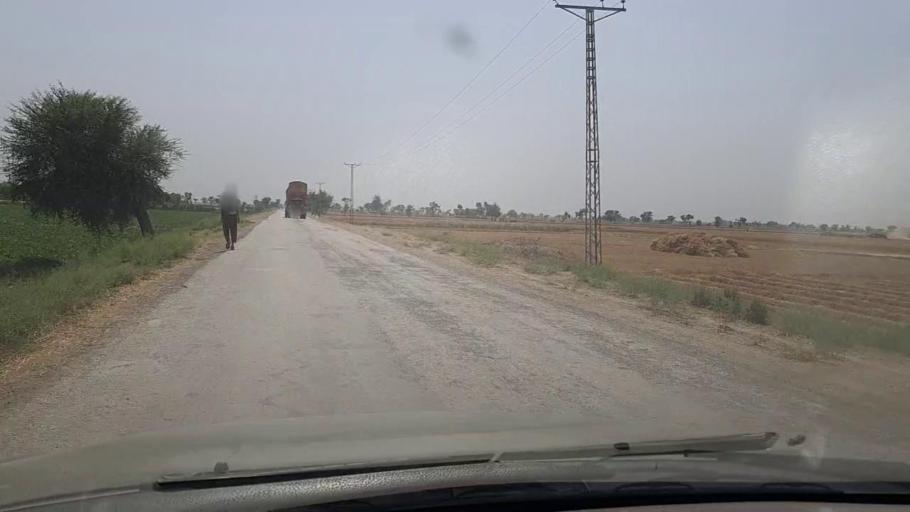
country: PK
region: Sindh
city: Miro Khan
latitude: 27.7151
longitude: 68.0666
